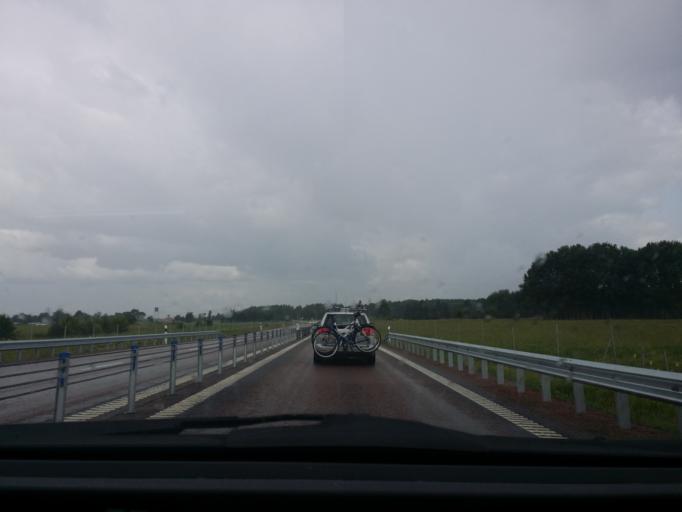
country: SE
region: Vaestmanland
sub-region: Hallstahammars Kommun
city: Kolback
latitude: 59.5898
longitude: 16.2614
